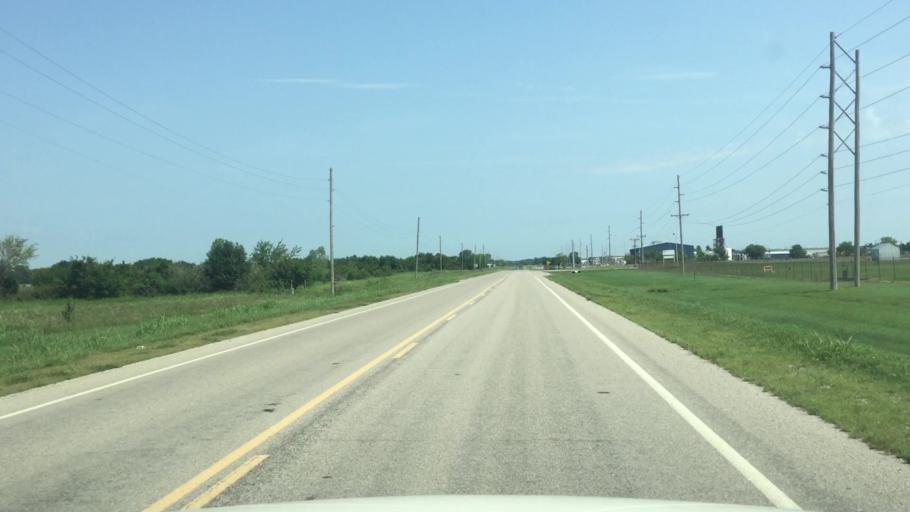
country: US
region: Kansas
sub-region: Montgomery County
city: Coffeyville
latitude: 37.0872
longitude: -95.5863
